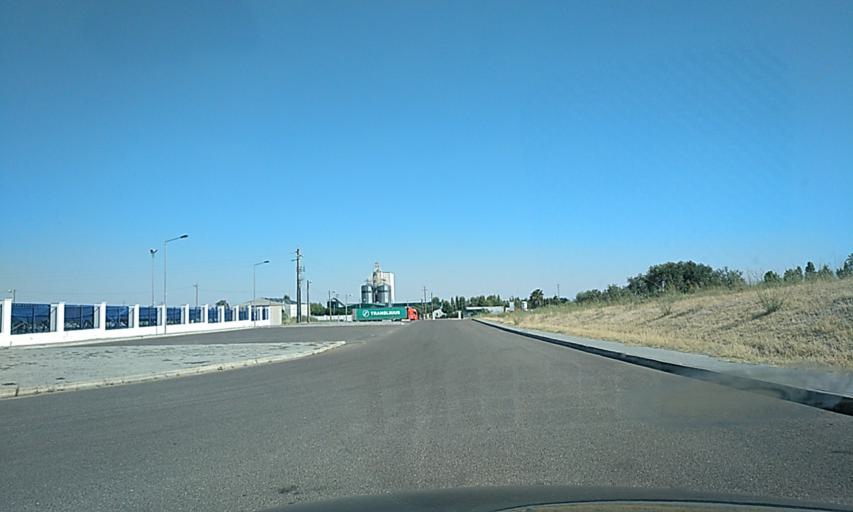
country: PT
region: Portalegre
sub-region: Campo Maior
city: Campo Maior
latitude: 39.0242
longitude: -7.0622
